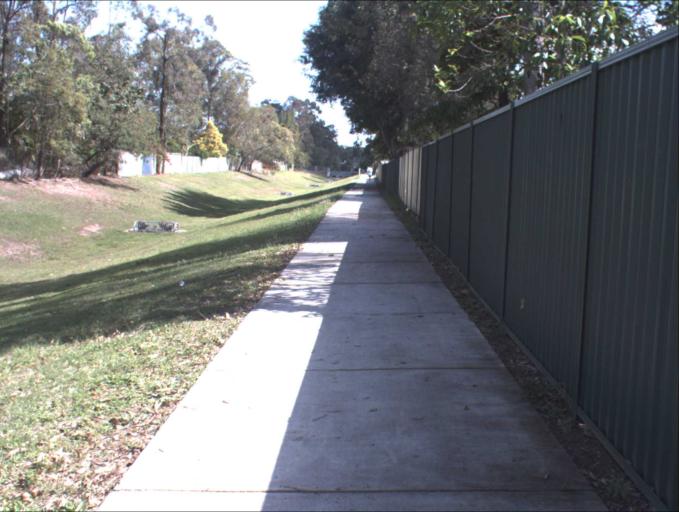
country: AU
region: Queensland
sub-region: Logan
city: Waterford West
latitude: -27.6749
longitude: 153.1115
